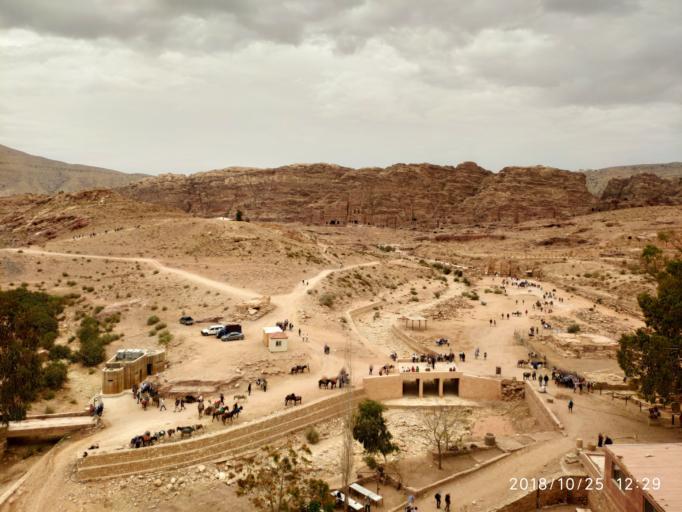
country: JO
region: Ma'an
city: Petra
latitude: 30.3305
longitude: 35.4394
